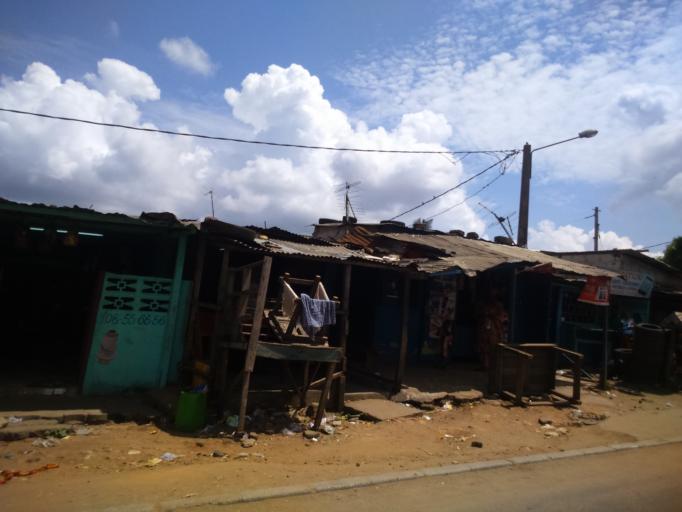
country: CI
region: Lagunes
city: Abidjan
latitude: 5.3533
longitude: -4.0875
